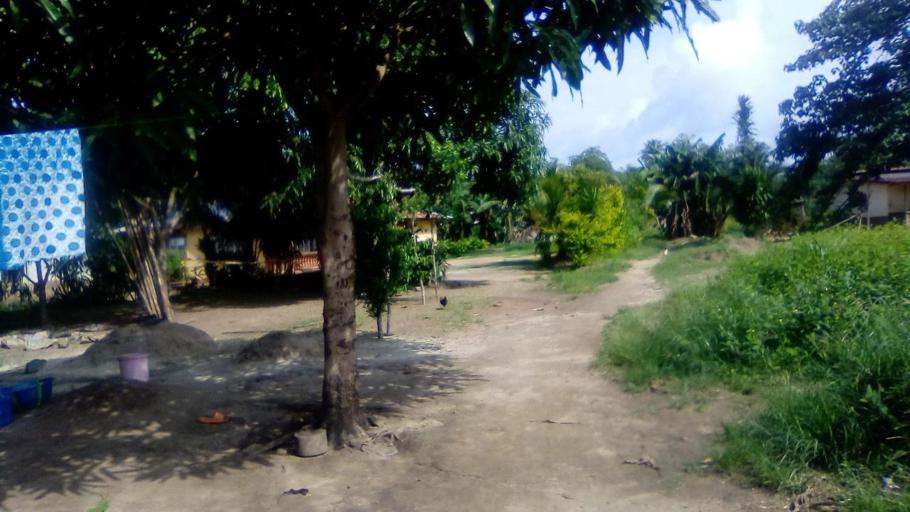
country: SL
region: Southern Province
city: Pujehun
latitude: 7.3672
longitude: -11.7281
